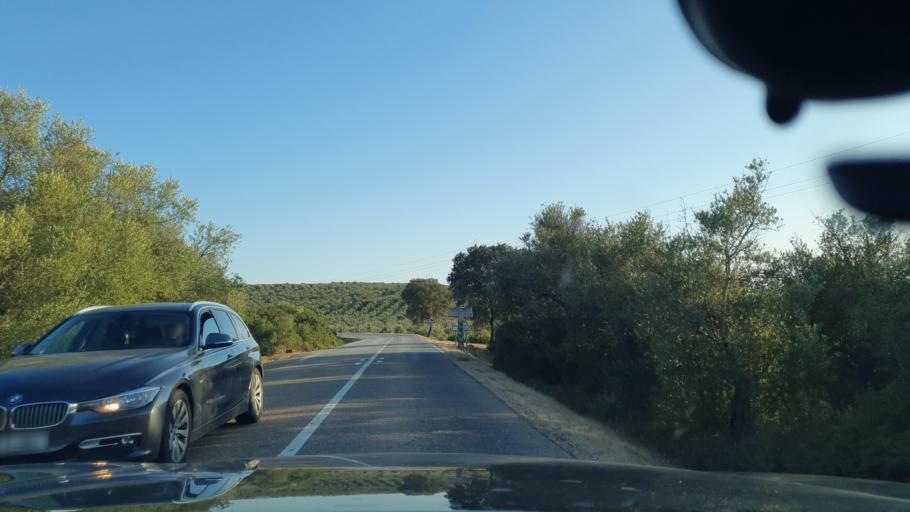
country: PT
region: Evora
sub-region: Estremoz
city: Estremoz
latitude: 38.9224
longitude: -7.6673
